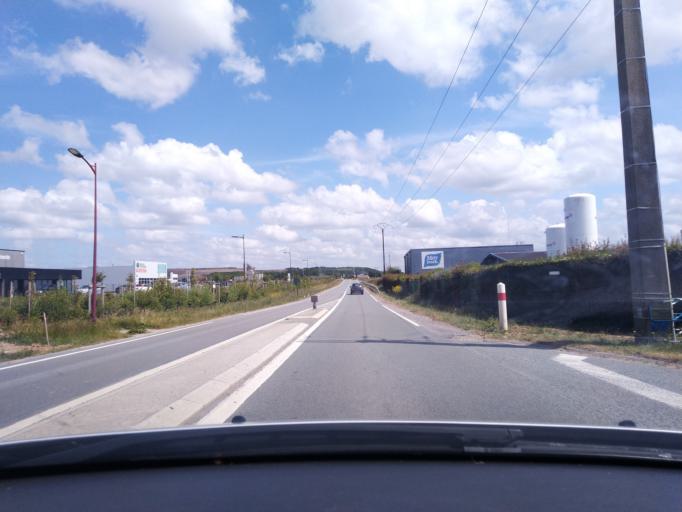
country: FR
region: Nord-Pas-de-Calais
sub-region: Departement du Pas-de-Calais
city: Marquise
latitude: 50.8238
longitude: 1.7144
